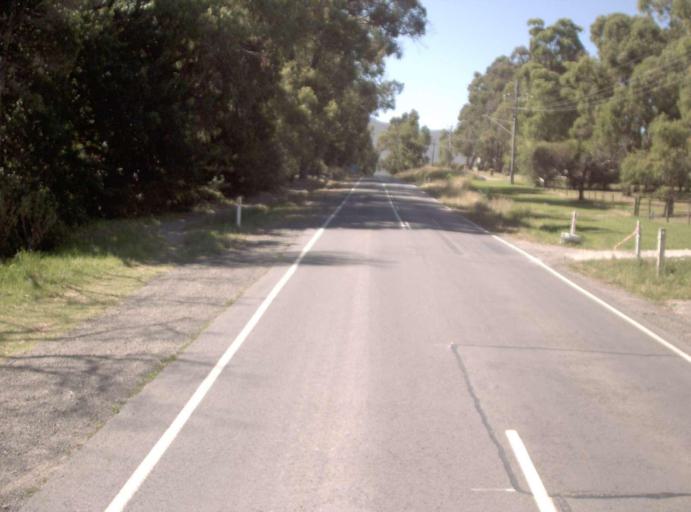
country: AU
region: Victoria
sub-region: Yarra Ranges
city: Healesville
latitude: -37.6709
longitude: 145.5376
